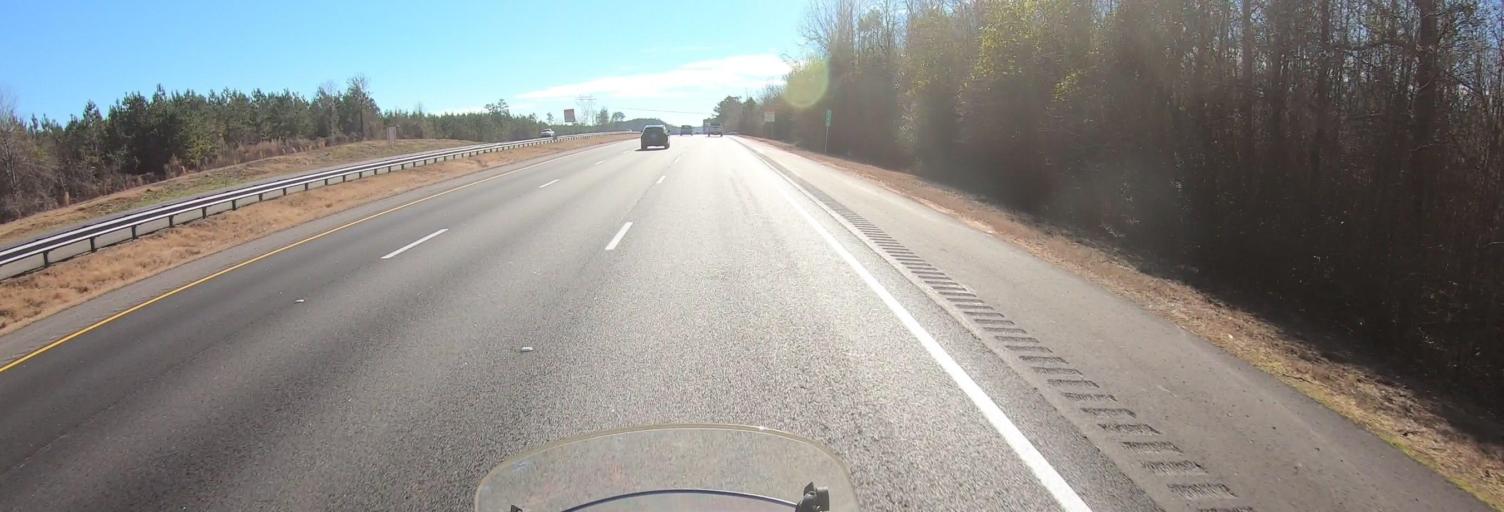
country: US
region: Georgia
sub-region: Monroe County
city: Forsyth
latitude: 33.1423
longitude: -84.0291
